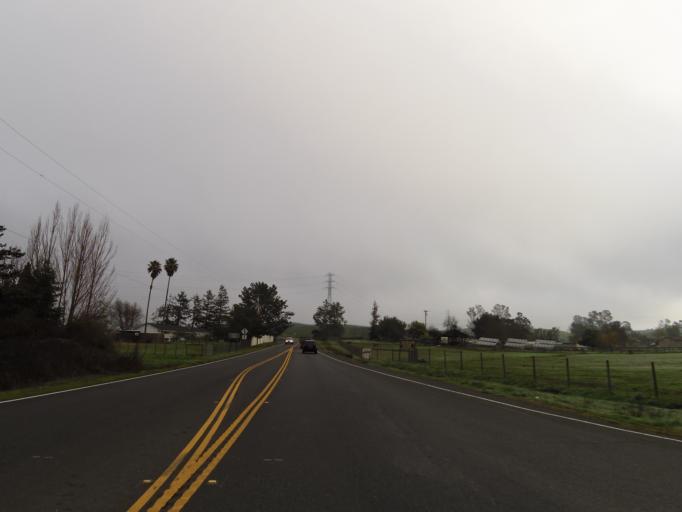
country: US
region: California
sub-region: Sonoma County
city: Sonoma
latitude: 38.2471
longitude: -122.4129
